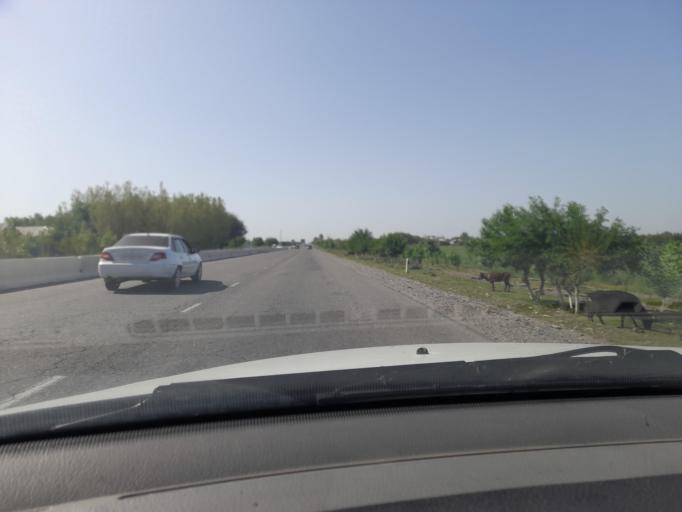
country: UZ
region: Samarqand
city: Daxbet
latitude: 39.8027
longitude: 66.8639
